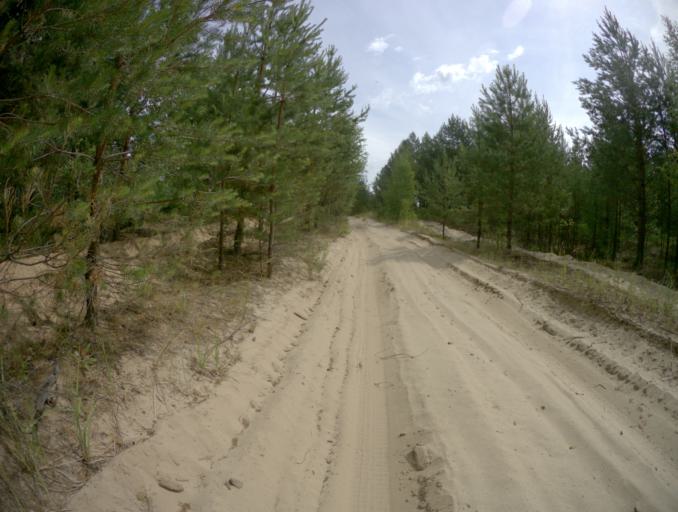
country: RU
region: Nizjnij Novgorod
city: Frolishchi
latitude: 56.4967
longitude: 42.5427
